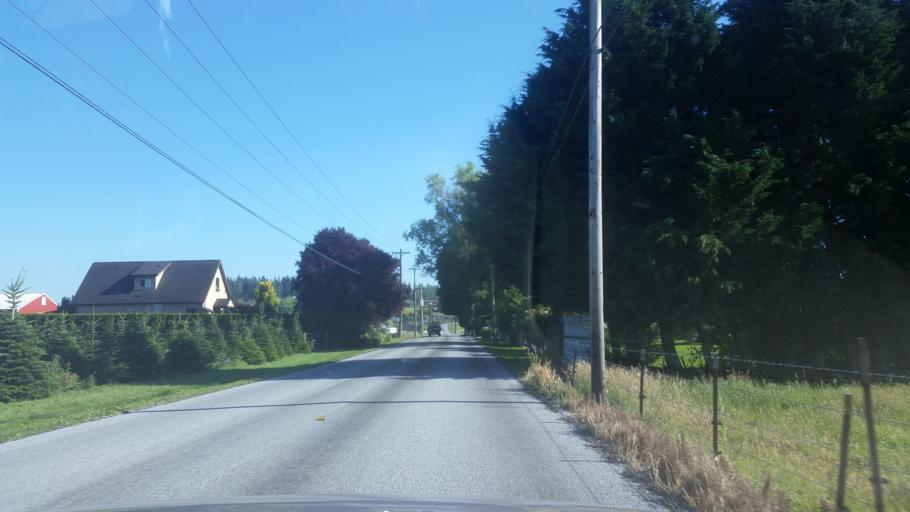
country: US
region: Washington
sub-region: Snohomish County
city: Snohomish
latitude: 47.8863
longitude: -122.0989
